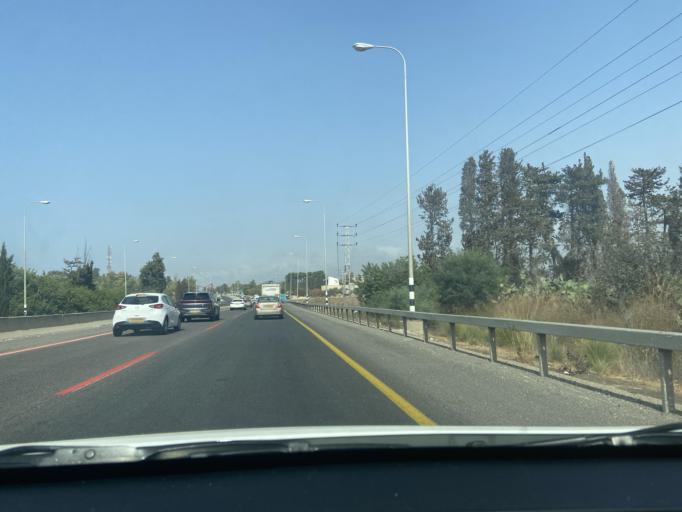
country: IL
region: Northern District
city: El Mazra`a
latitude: 32.9566
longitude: 35.0920
